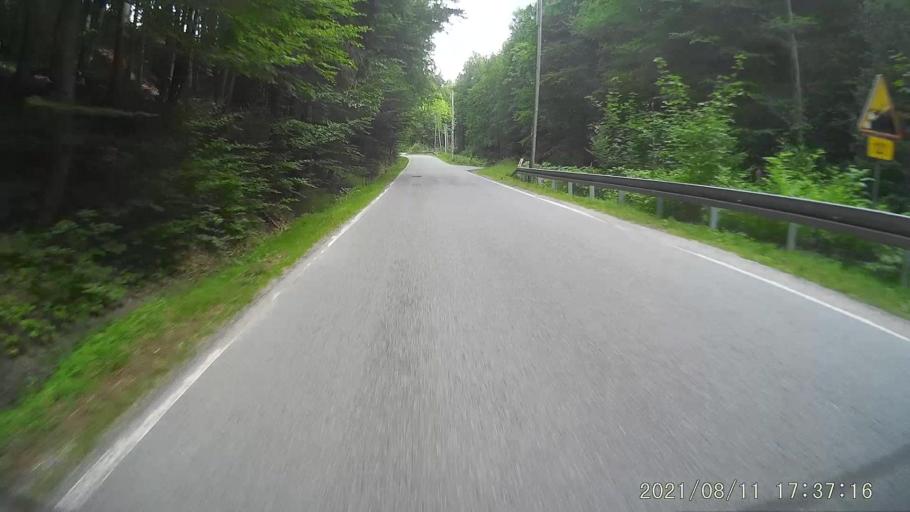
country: PL
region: Lower Silesian Voivodeship
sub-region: Powiat klodzki
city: Duszniki-Zdroj
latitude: 50.3370
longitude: 16.4051
